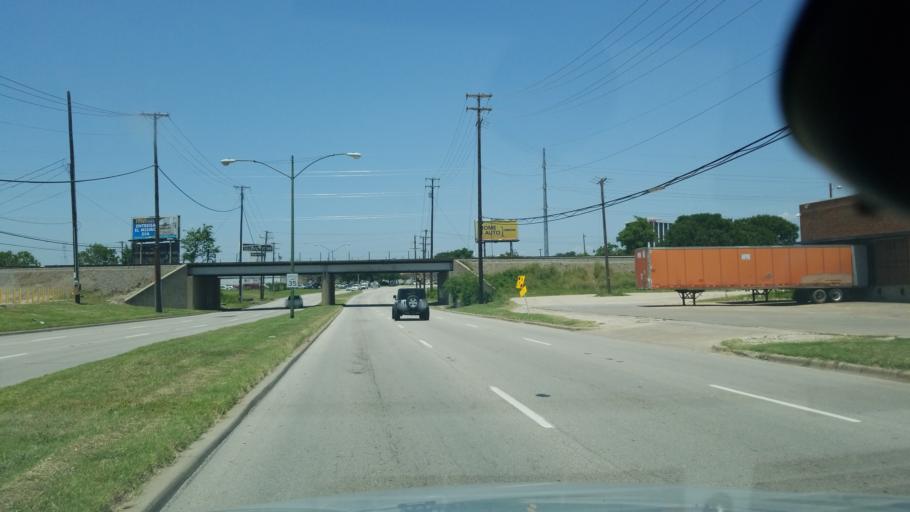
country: US
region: Texas
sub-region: Dallas County
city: Dallas
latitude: 32.8125
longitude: -96.8736
